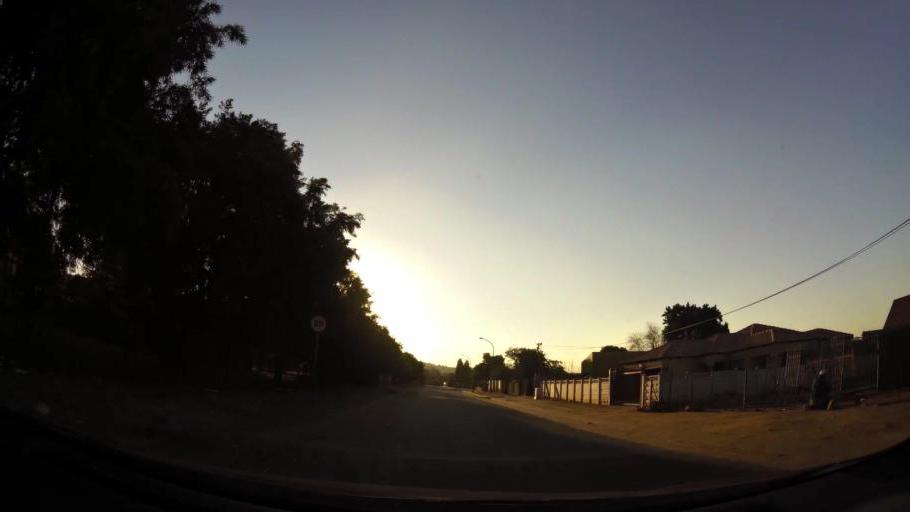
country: ZA
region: North-West
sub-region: Bojanala Platinum District Municipality
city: Rustenburg
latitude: -25.6411
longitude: 27.2079
